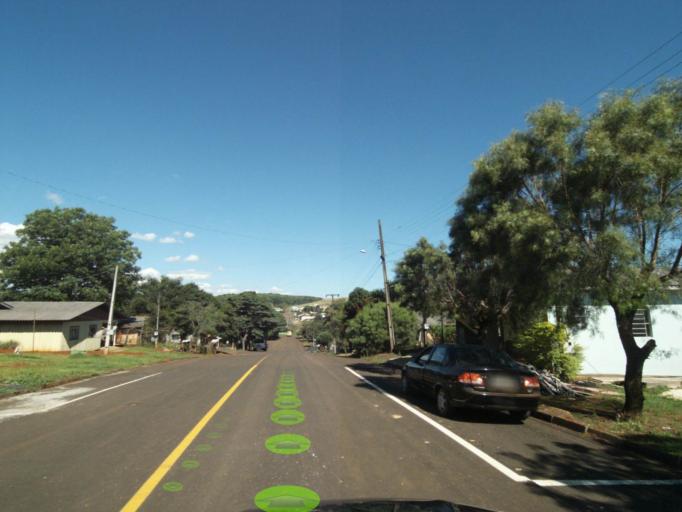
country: BR
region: Parana
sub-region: Coronel Vivida
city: Coronel Vivida
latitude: -26.1441
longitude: -52.3889
